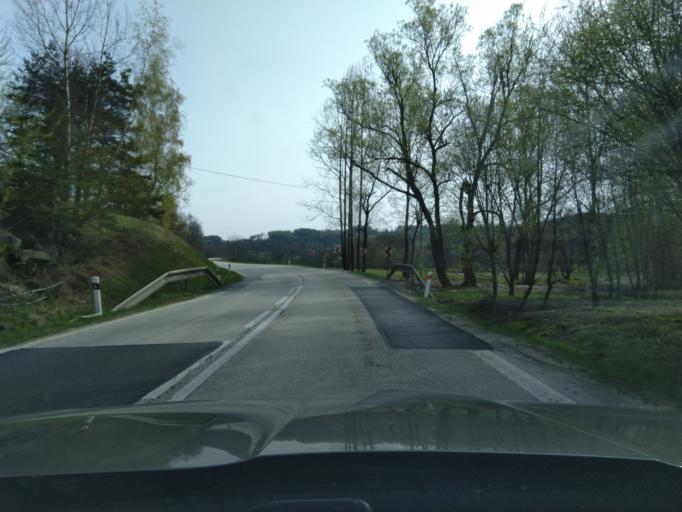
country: CZ
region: Jihocesky
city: Ckyne
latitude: 49.0945
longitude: 13.7983
